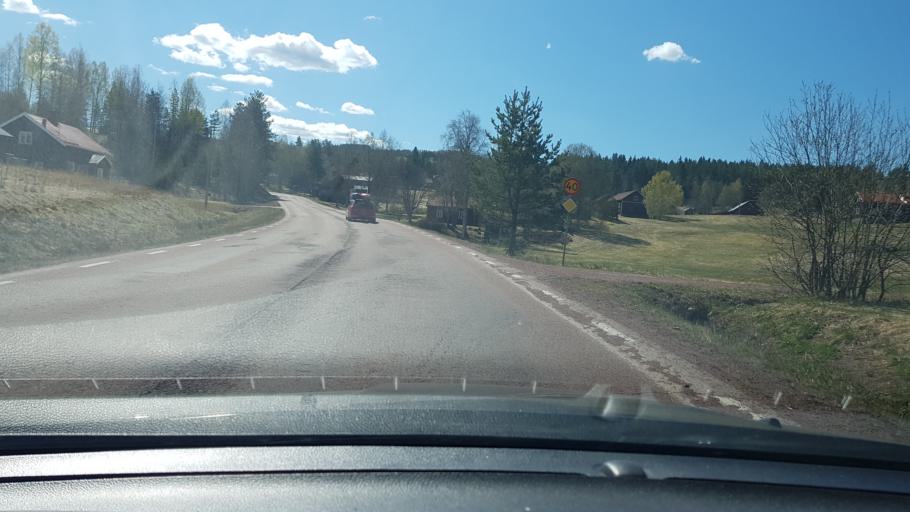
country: SE
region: Dalarna
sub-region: Alvdalens Kommun
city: AElvdalen
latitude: 61.1193
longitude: 14.1708
